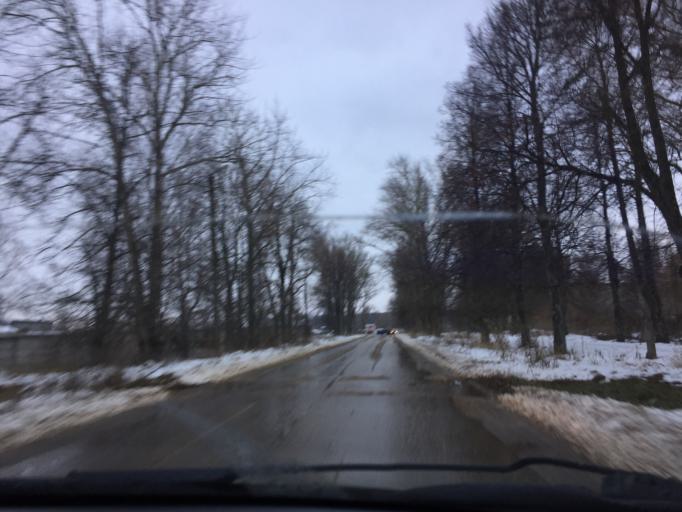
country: RU
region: Tula
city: Lomintsevskiy
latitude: 53.9383
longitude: 37.6498
